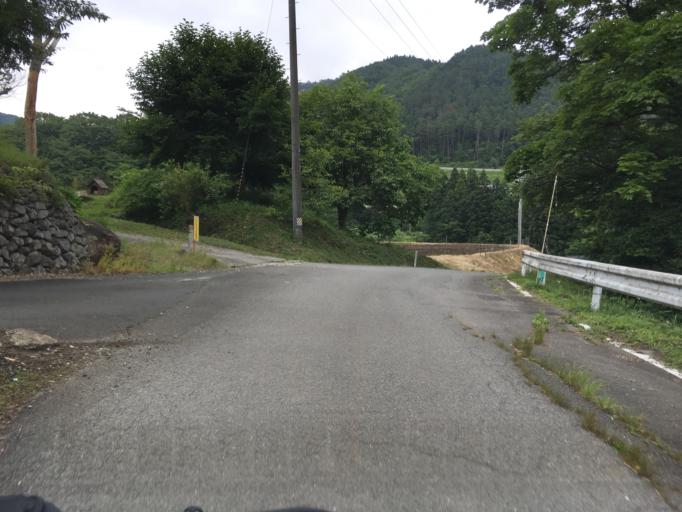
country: JP
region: Miyagi
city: Marumori
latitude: 37.7755
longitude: 140.8305
